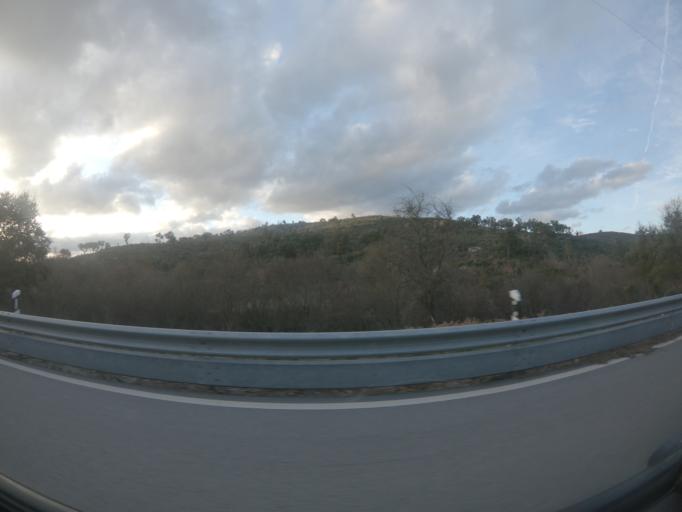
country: PT
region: Braganca
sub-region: Carrazeda de Ansiaes
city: Carrazeda de Anciaes
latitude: 41.2051
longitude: -7.3375
